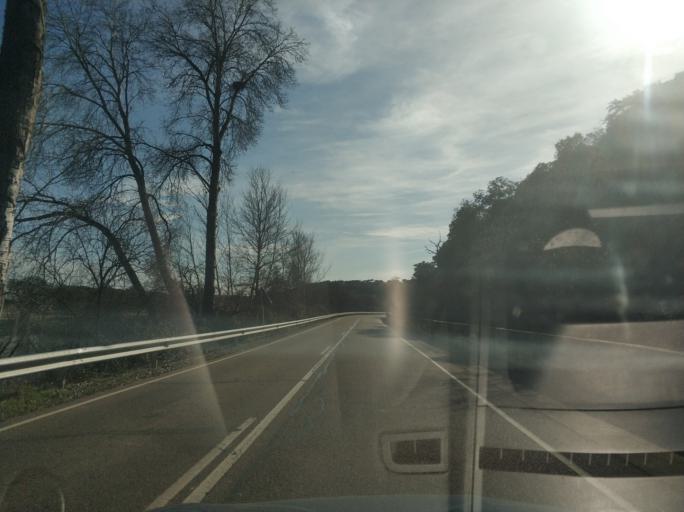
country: ES
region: Castille and Leon
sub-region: Provincia de Salamanca
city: Carrascal de Barregas
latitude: 40.9973
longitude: -5.7323
